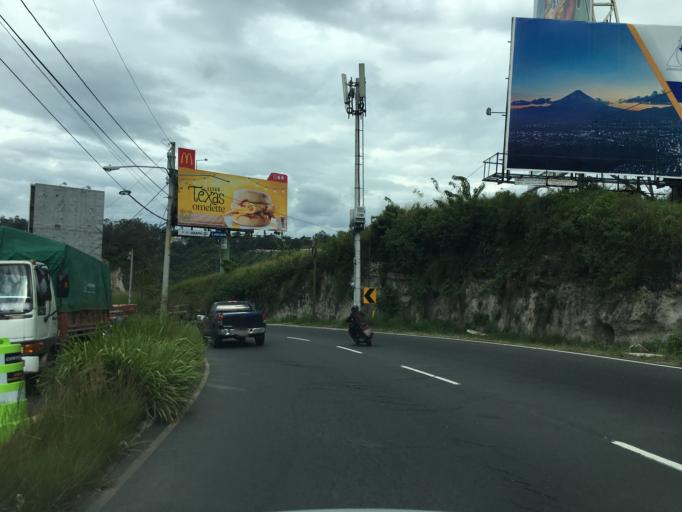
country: GT
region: Guatemala
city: Mixco
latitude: 14.5900
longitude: -90.5751
